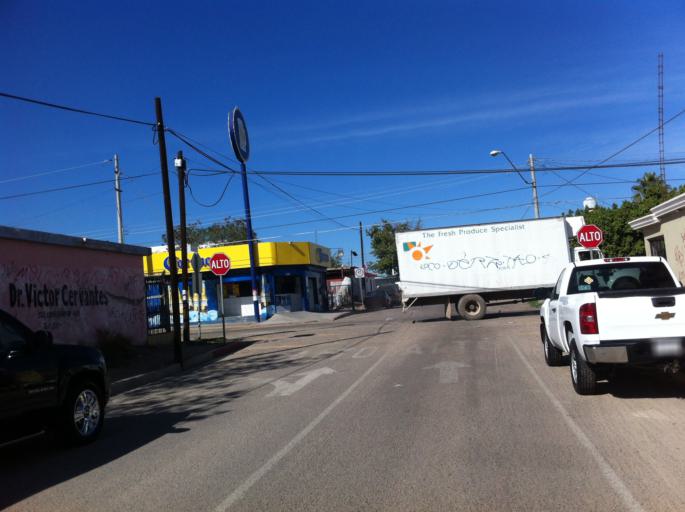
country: MX
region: Sonora
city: Hermosillo
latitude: 29.1031
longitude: -111.0113
